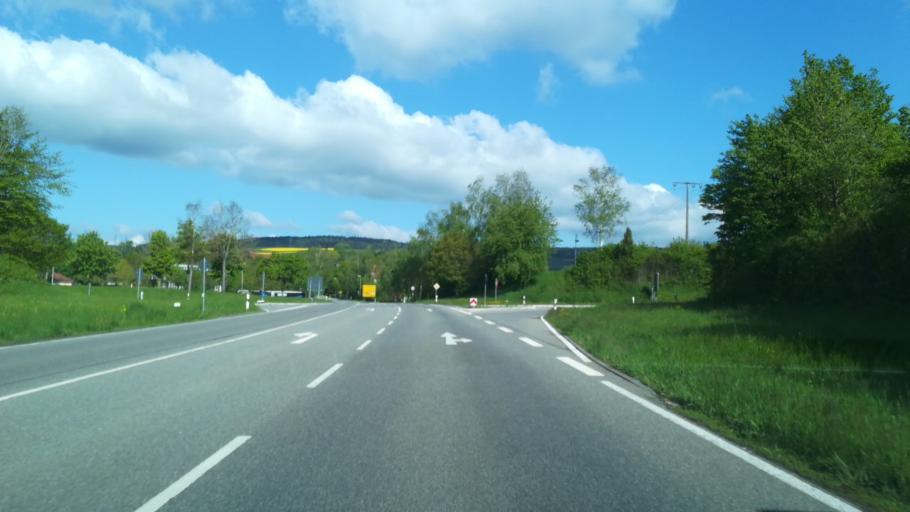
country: DE
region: Baden-Wuerttemberg
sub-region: Freiburg Region
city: Tengen
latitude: 47.8161
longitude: 8.6639
